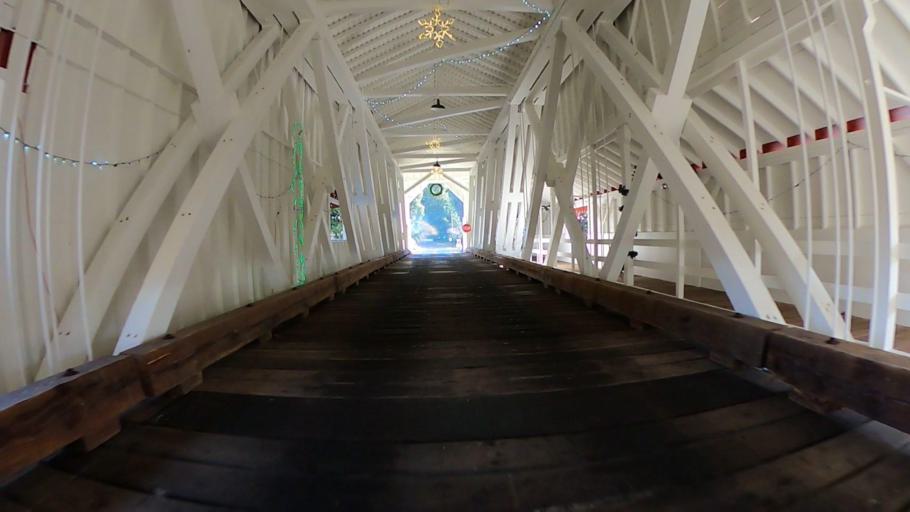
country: US
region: Oregon
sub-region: Lane County
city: Oakridge
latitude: 43.7586
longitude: -122.4957
